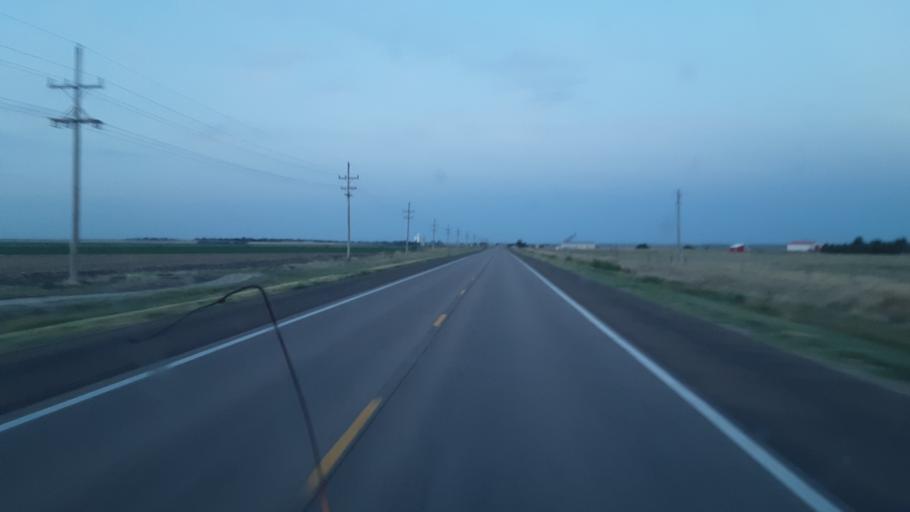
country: US
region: Kansas
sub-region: Kearny County
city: Lakin
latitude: 37.9736
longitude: -101.1762
